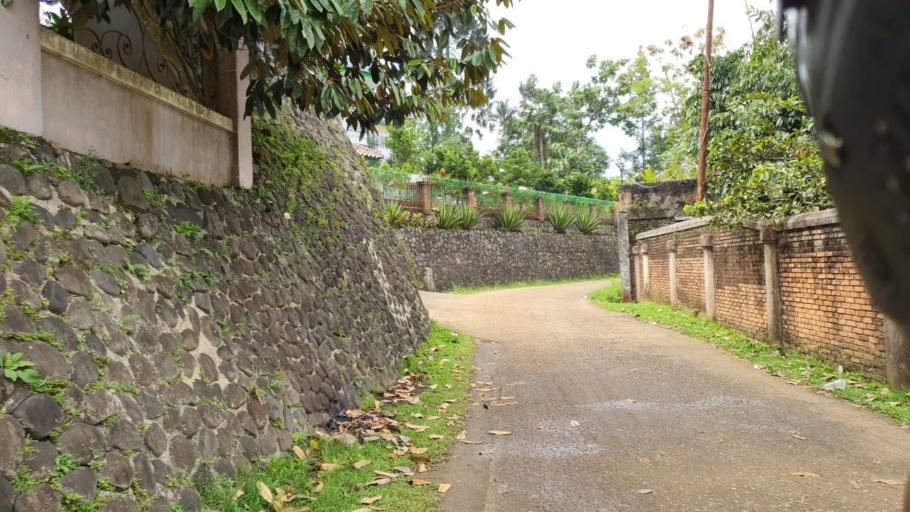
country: ID
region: West Java
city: Caringin
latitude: -6.6537
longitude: 106.8844
